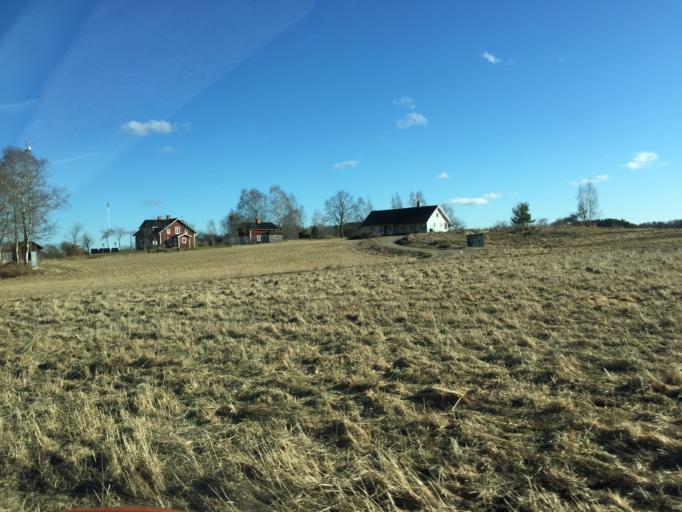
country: SE
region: Soedermanland
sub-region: Vingakers Kommun
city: Vingaker
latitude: 58.9373
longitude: 15.8711
